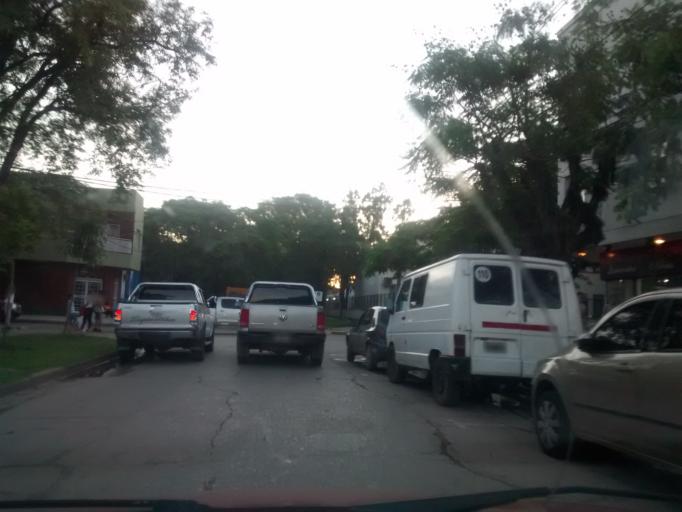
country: AR
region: Chaco
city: Resistencia
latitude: -27.4517
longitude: -58.9924
